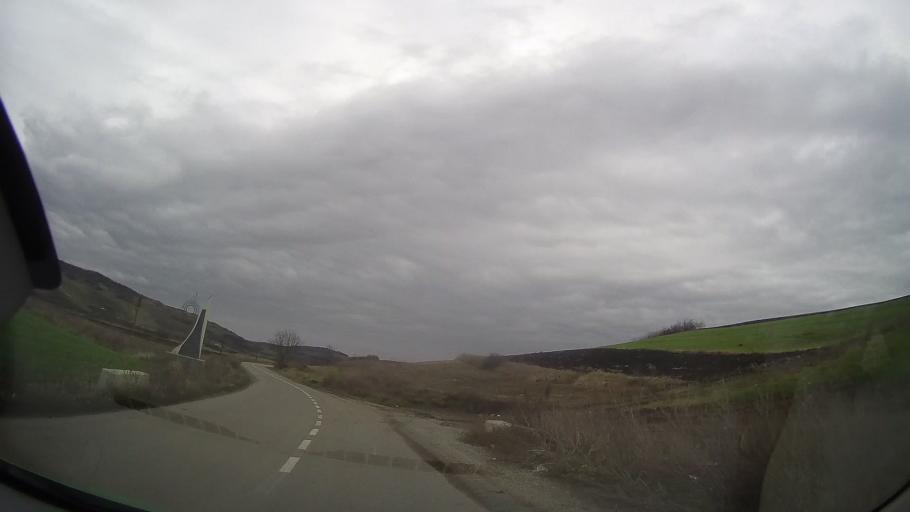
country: RO
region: Mures
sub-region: Comuna Craesti
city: Craiesti
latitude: 46.7766
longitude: 24.4255
